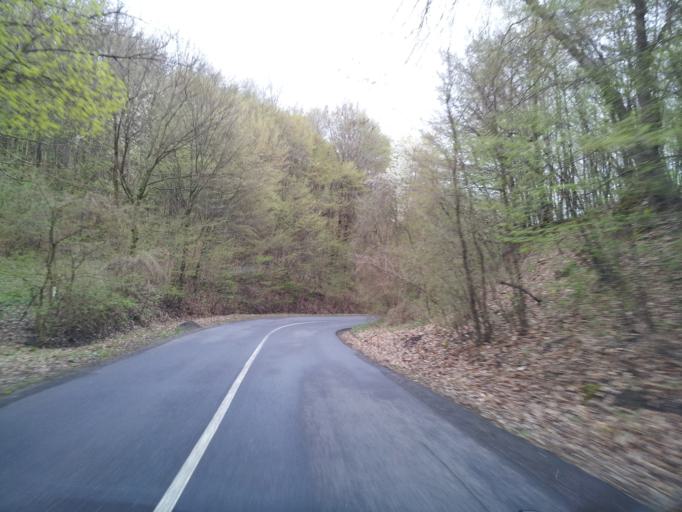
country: HU
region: Borsod-Abauj-Zemplen
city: Rudabanya
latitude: 48.4772
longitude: 20.5455
